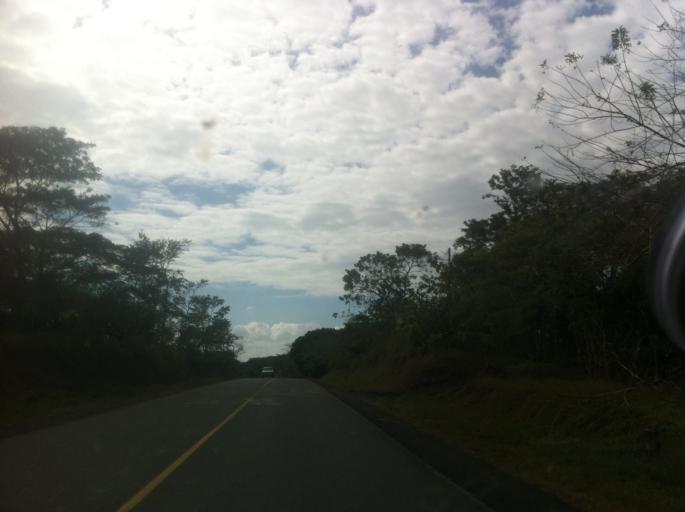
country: NI
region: Rio San Juan
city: San Miguelito
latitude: 11.3332
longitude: -84.7494
